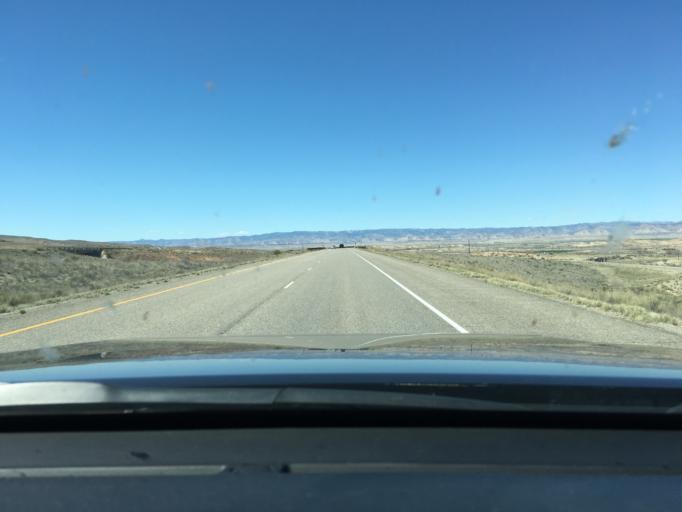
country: US
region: Colorado
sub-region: Mesa County
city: Loma
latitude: 39.2128
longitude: -108.8658
